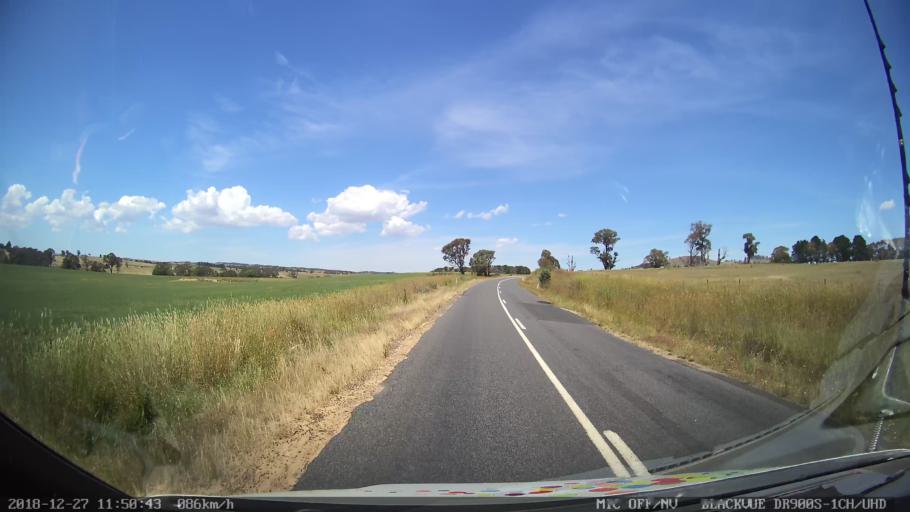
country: AU
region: New South Wales
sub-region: Bathurst Regional
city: Perthville
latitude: -33.6349
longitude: 149.4283
